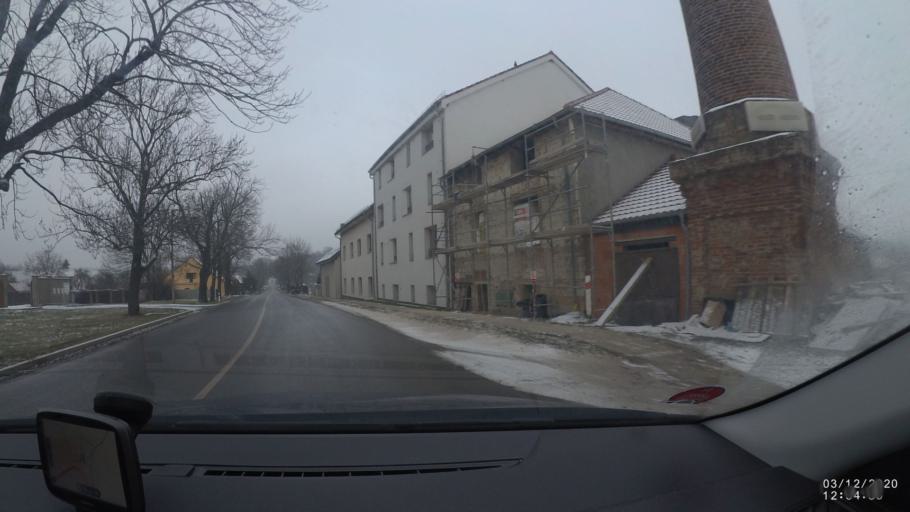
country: CZ
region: Central Bohemia
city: Revnicov
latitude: 50.1869
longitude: 13.8117
